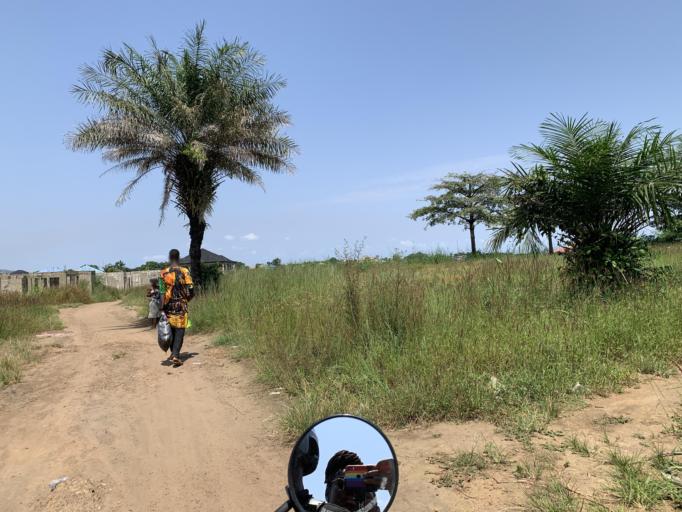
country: SL
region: Western Area
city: Hastings
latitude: 8.3960
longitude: -13.1328
